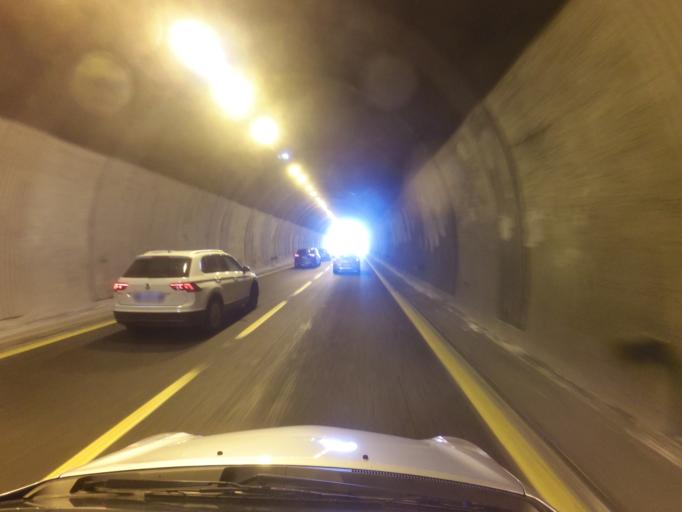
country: IT
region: Tuscany
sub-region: Province of Florence
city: Calenzano
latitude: 43.8691
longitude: 11.1743
